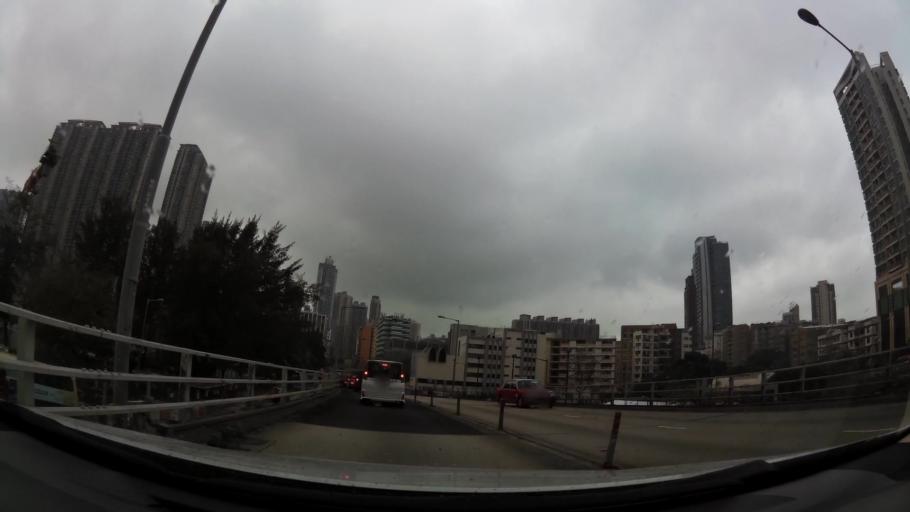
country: HK
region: Kowloon City
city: Kowloon
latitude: 22.3268
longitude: 114.1900
